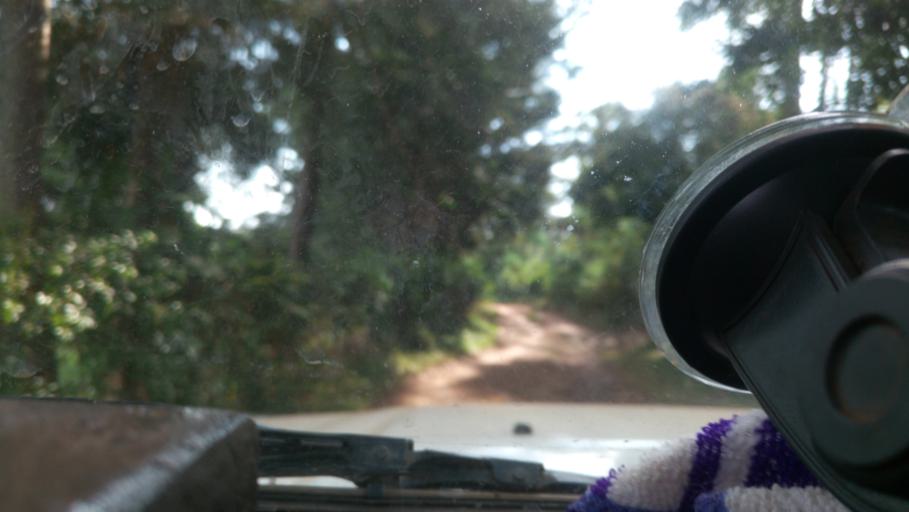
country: KE
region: Kericho
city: Litein
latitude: -0.4559
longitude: 35.1287
